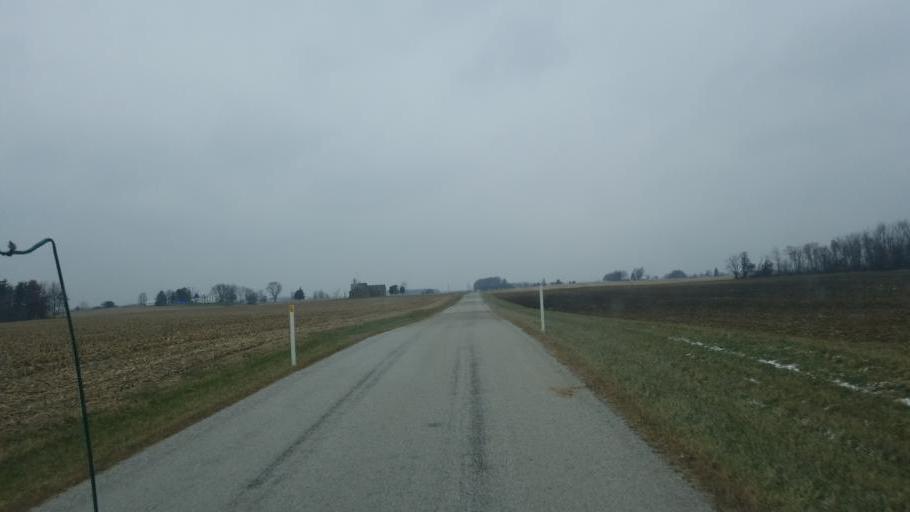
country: US
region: Ohio
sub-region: Richland County
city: Shelby
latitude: 40.8832
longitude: -82.7151
